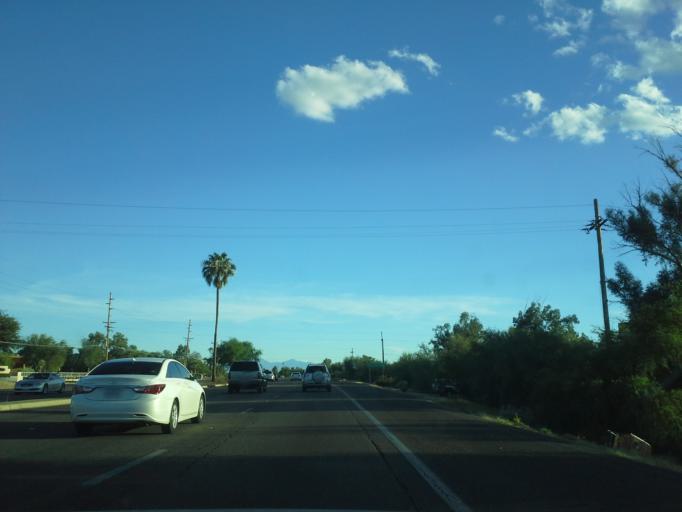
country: US
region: Arizona
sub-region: Pima County
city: Casas Adobes
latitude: 32.3345
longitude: -110.9775
